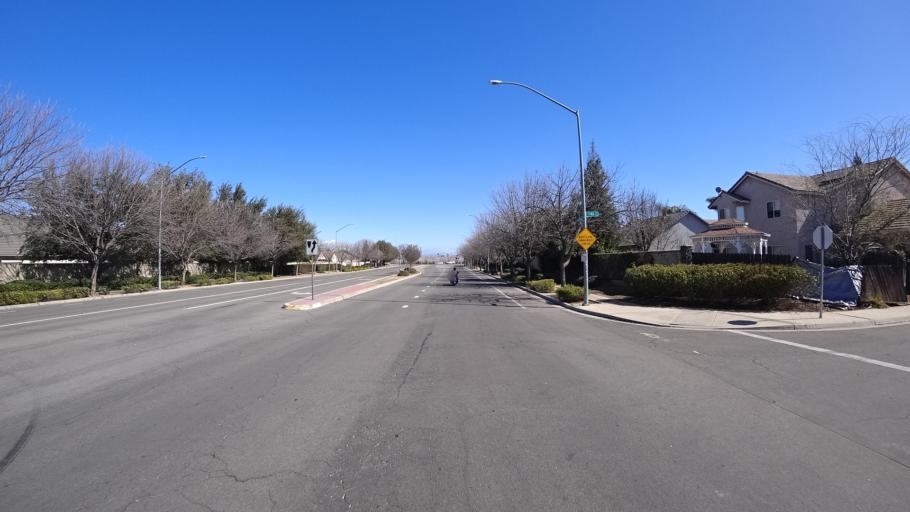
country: US
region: California
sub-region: Fresno County
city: Clovis
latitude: 36.8740
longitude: -119.7323
